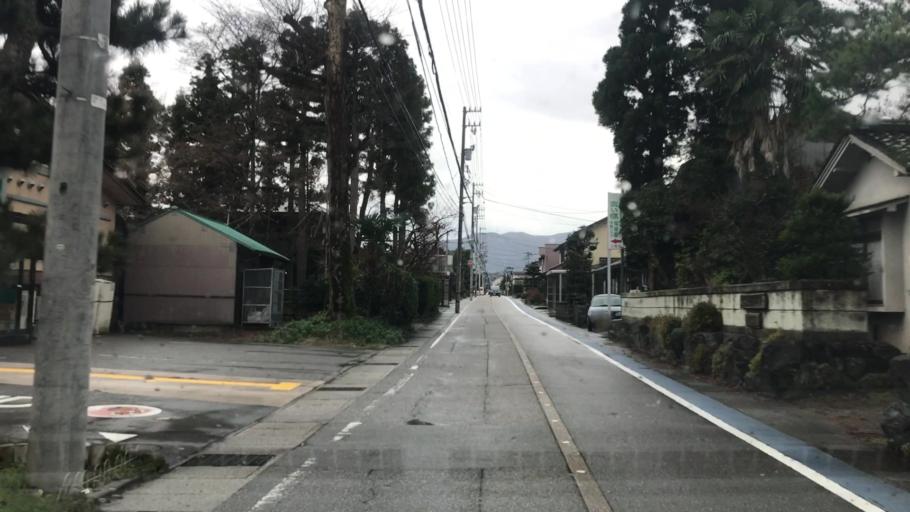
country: JP
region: Toyama
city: Yatsuomachi-higashikumisaka
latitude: 36.5977
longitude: 137.2061
